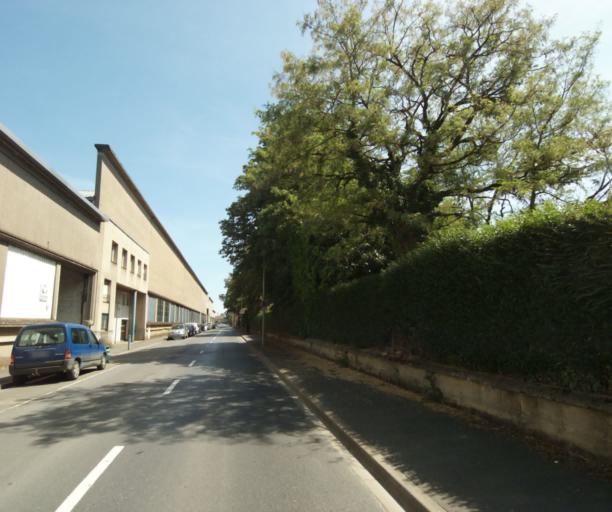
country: FR
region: Champagne-Ardenne
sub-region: Departement des Ardennes
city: Charleville-Mezieres
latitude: 49.7682
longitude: 4.7108
